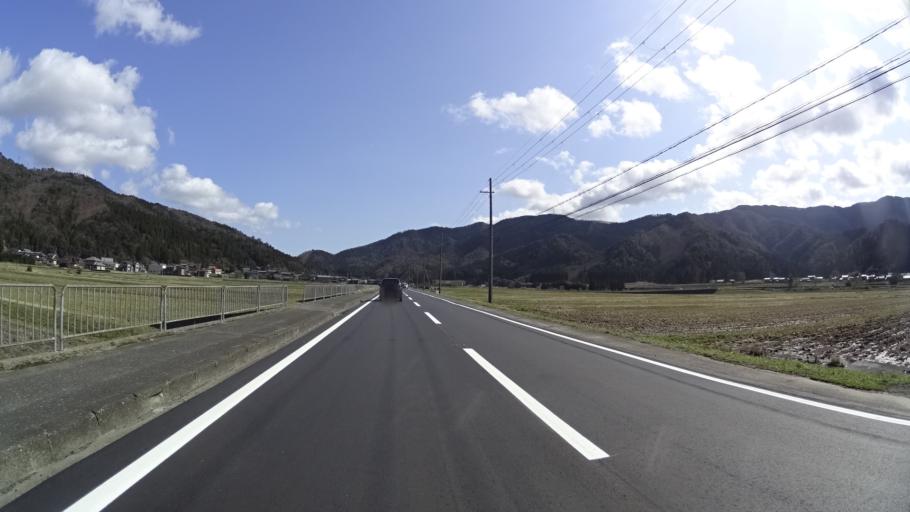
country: JP
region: Fukui
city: Obama
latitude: 35.4582
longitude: 135.8769
